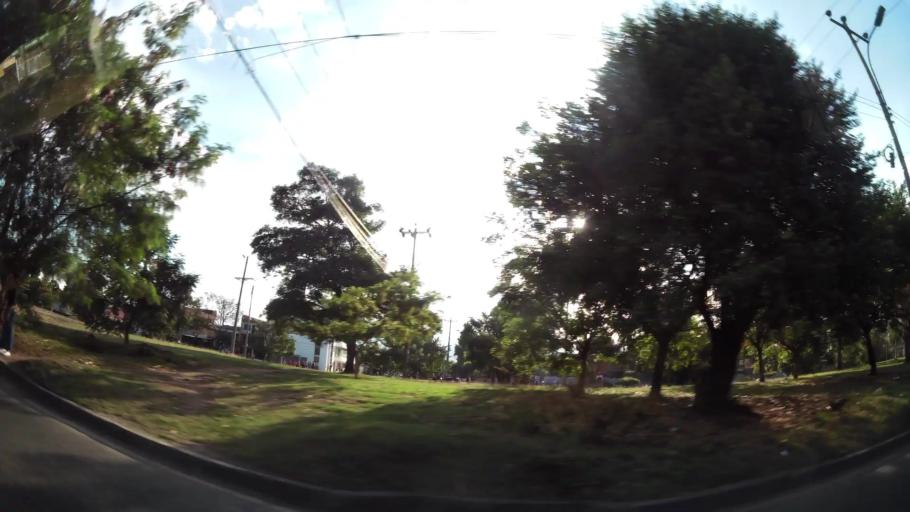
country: CO
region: Valle del Cauca
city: Cali
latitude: 3.4831
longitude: -76.4897
